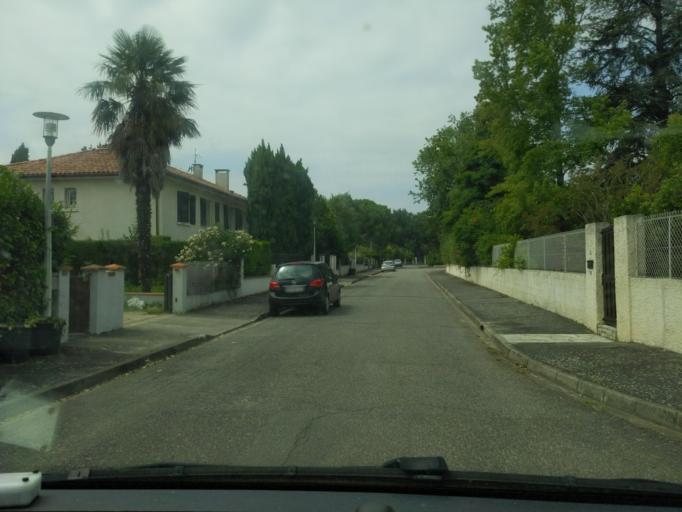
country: FR
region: Midi-Pyrenees
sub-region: Departement de la Haute-Garonne
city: Labege
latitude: 43.5305
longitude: 1.5427
